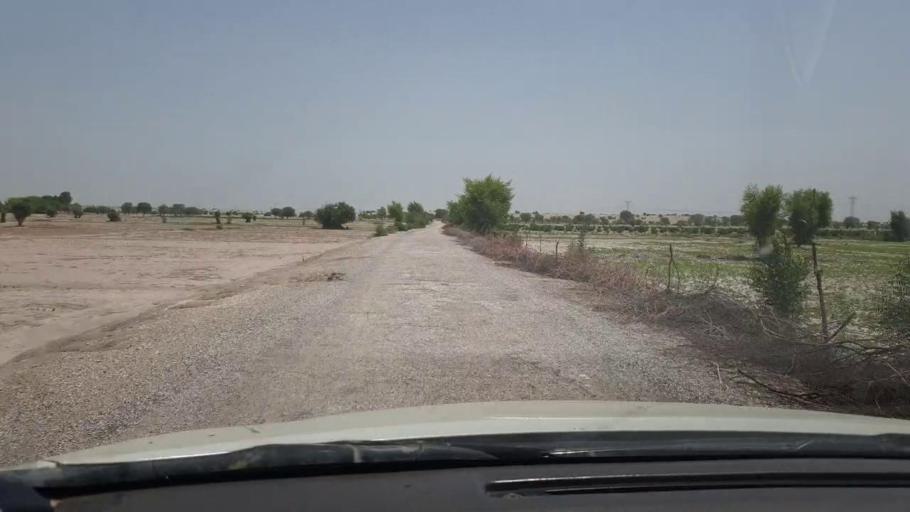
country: PK
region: Sindh
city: Rohri
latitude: 27.5062
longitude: 69.1741
